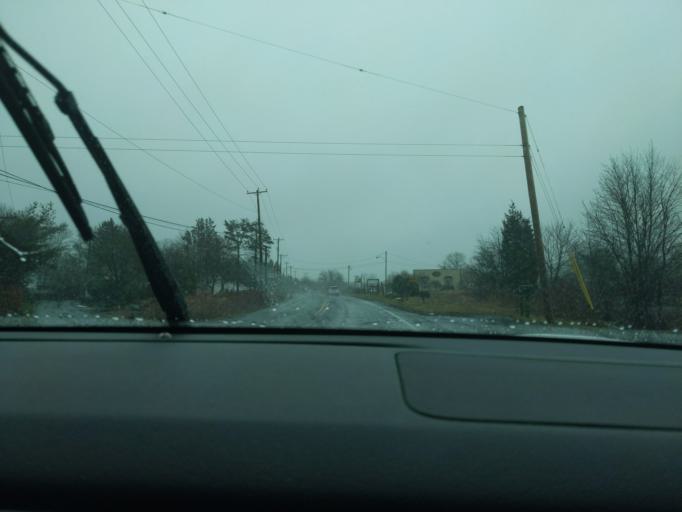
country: US
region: Pennsylvania
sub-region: Bucks County
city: Dublin
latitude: 40.3638
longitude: -75.1902
